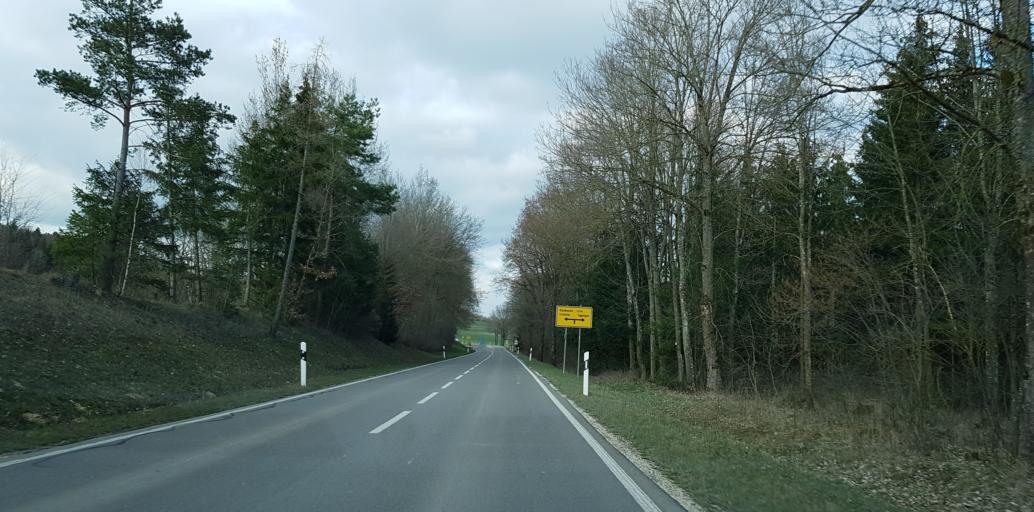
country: DE
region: Baden-Wuerttemberg
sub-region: Tuebingen Region
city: Erbach
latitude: 48.3514
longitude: 9.8556
